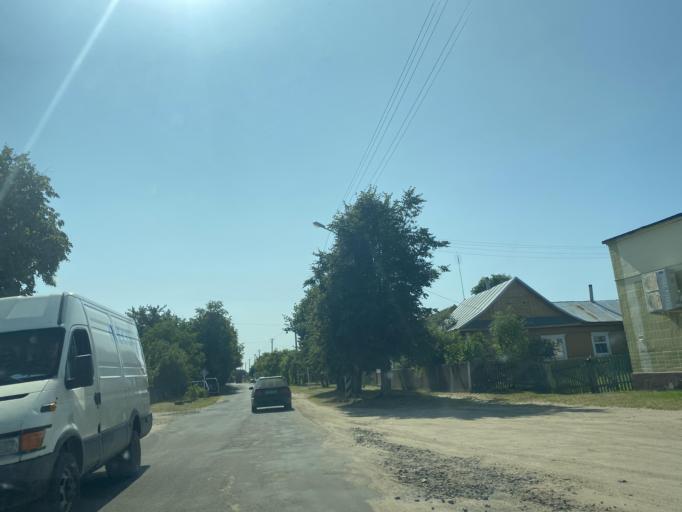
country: BY
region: Brest
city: Ivanava
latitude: 52.3130
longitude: 25.6164
